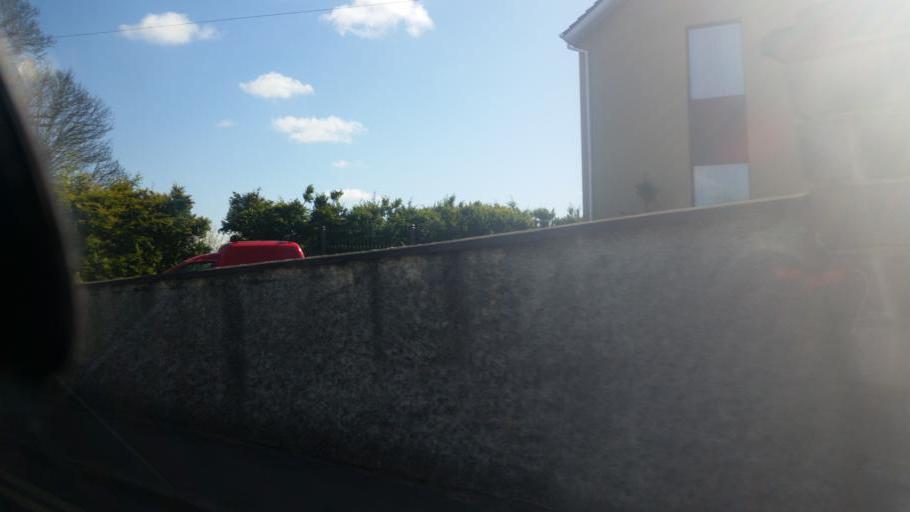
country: IE
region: Munster
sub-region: Waterford
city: Waterford
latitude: 52.2670
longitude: -7.1068
